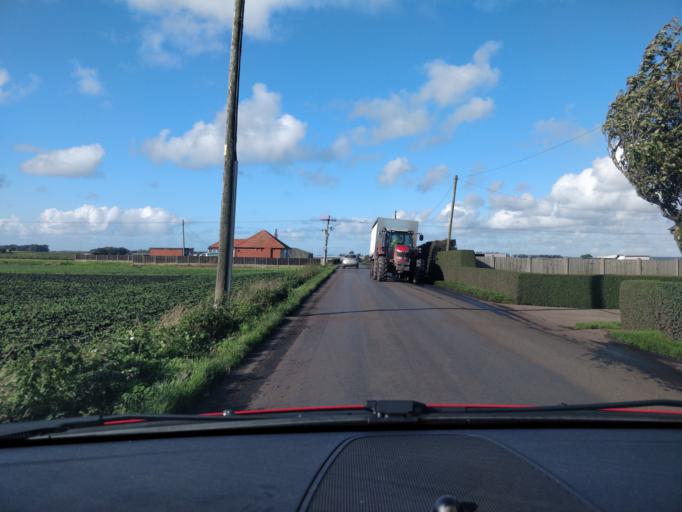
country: GB
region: England
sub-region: Lancashire
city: Banks
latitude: 53.6839
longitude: -2.8765
